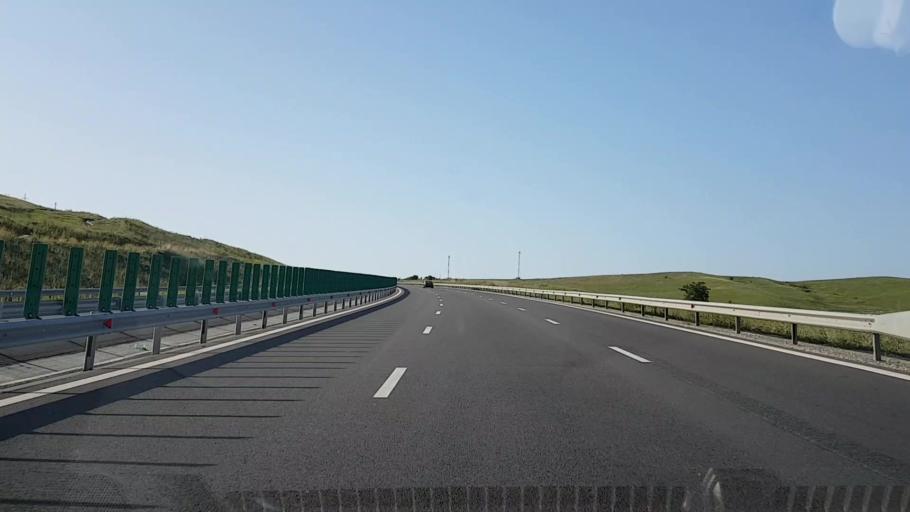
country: RO
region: Cluj
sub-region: Comuna Mihai Viteazu
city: Mihai Viteazu
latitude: 46.4939
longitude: 23.7810
